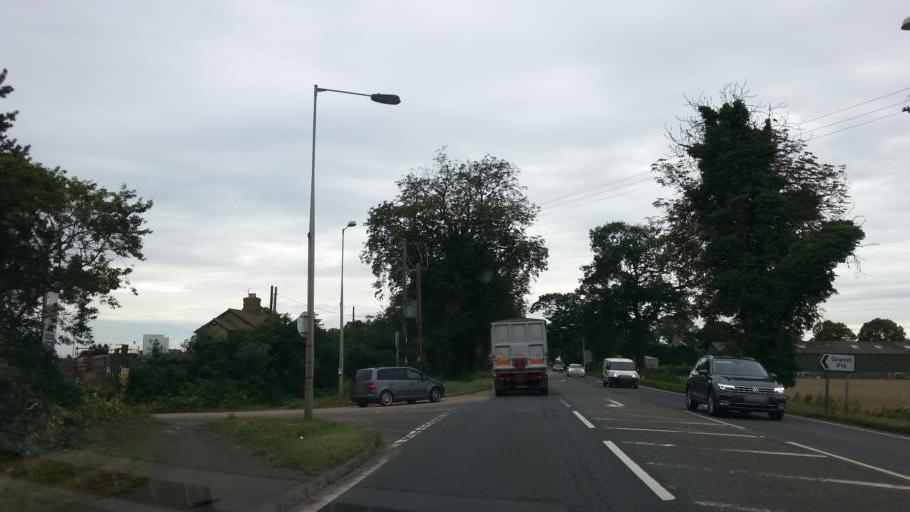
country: GB
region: England
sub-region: Peterborough
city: Thorney
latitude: 52.6174
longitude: -0.1404
